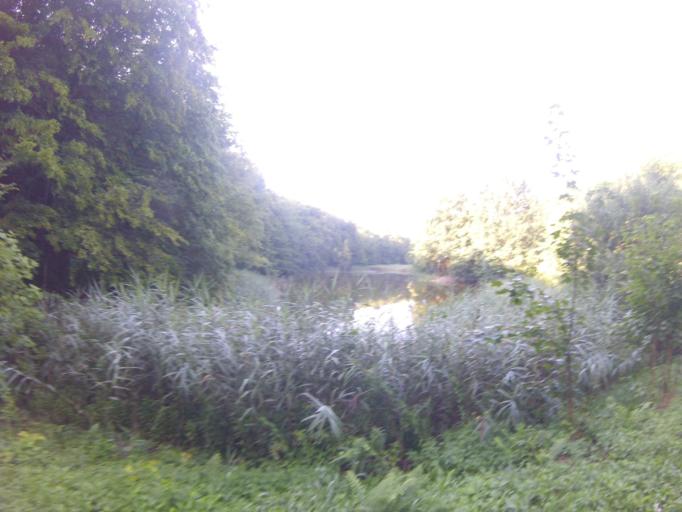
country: HU
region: Zala
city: Letenye
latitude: 46.5075
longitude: 16.7163
